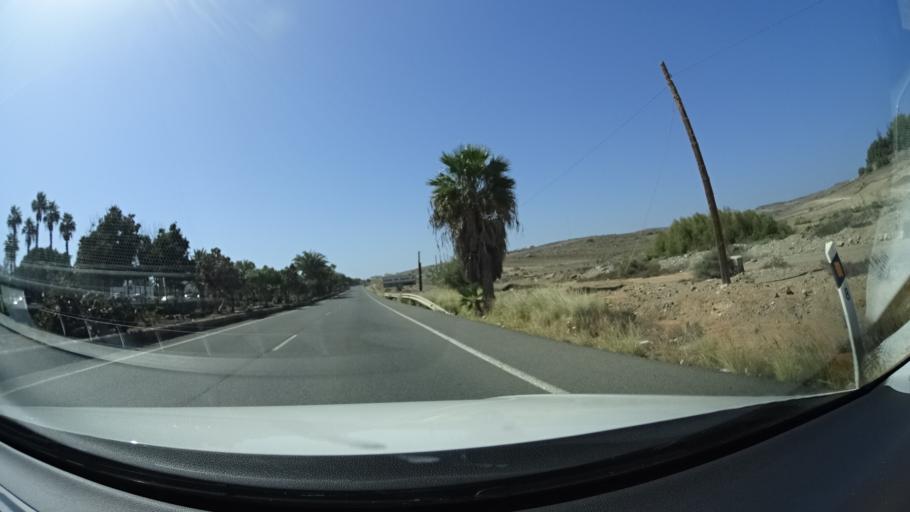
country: ES
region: Canary Islands
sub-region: Provincia de Las Palmas
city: Playa del Ingles
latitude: 27.7809
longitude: -15.5223
